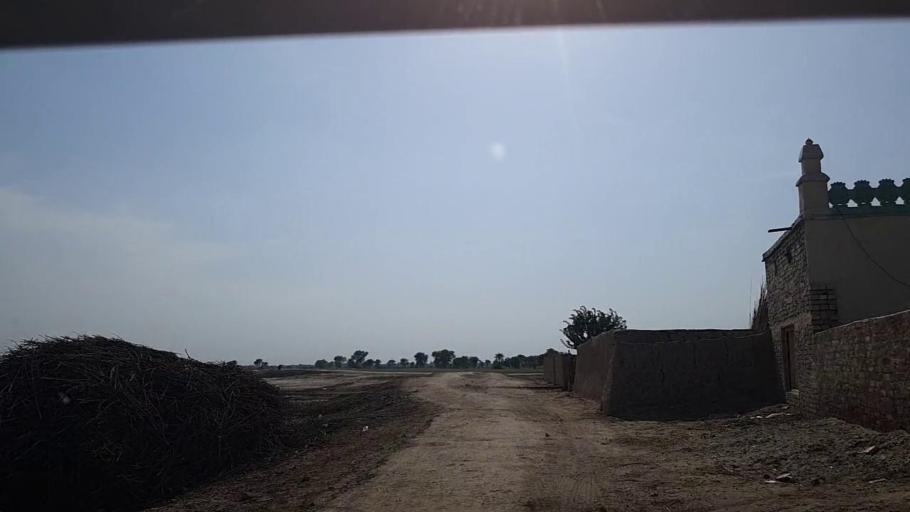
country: PK
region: Sindh
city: Khanpur
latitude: 27.8418
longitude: 69.3308
